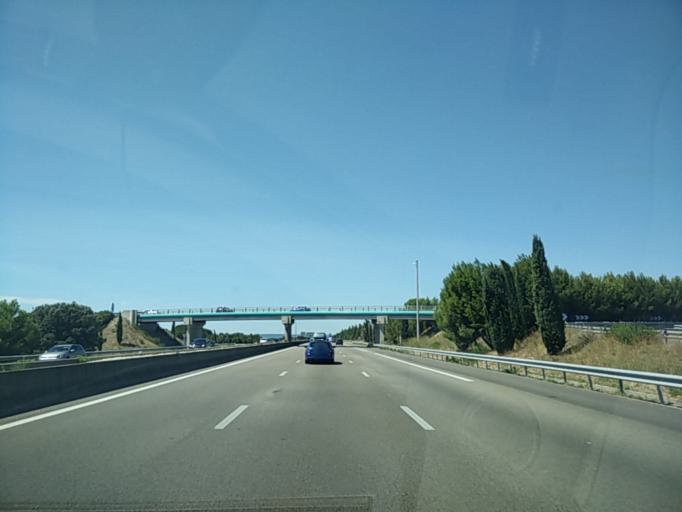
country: FR
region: Provence-Alpes-Cote d'Azur
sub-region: Departement du Vaucluse
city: Courthezon
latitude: 44.1098
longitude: 4.8448
